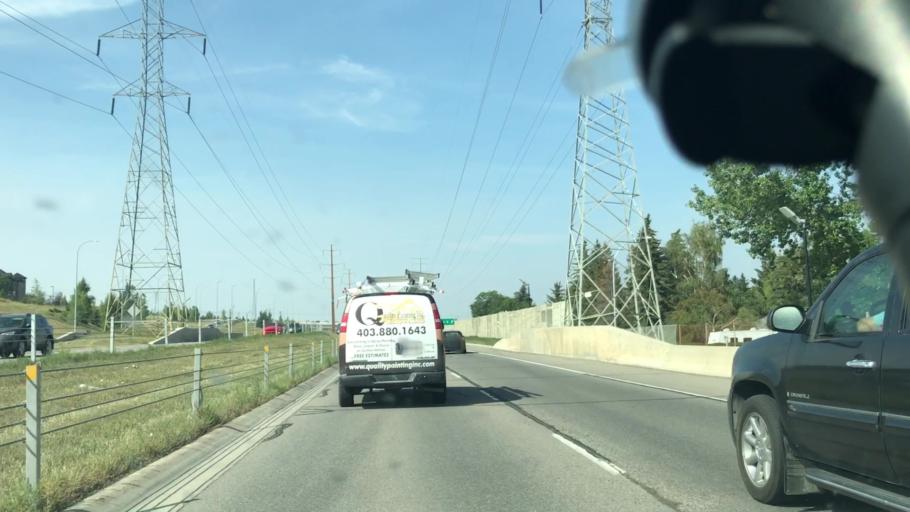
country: CA
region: Alberta
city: Calgary
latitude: 51.0346
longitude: -114.1642
